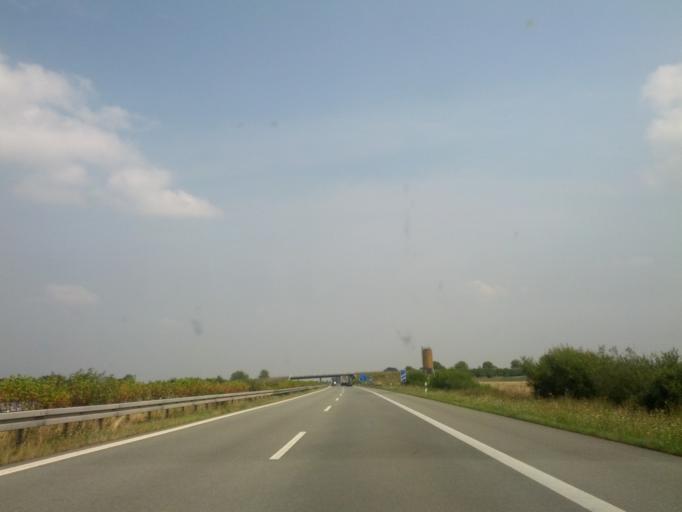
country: DE
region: Mecklenburg-Vorpommern
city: Bad Sulze
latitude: 54.0581
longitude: 12.6648
